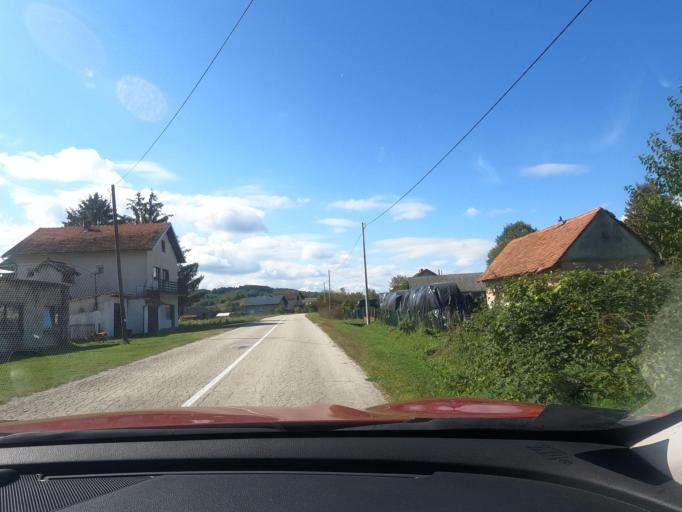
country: BA
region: Federation of Bosnia and Herzegovina
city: Podzvizd
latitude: 45.2294
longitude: 15.9150
